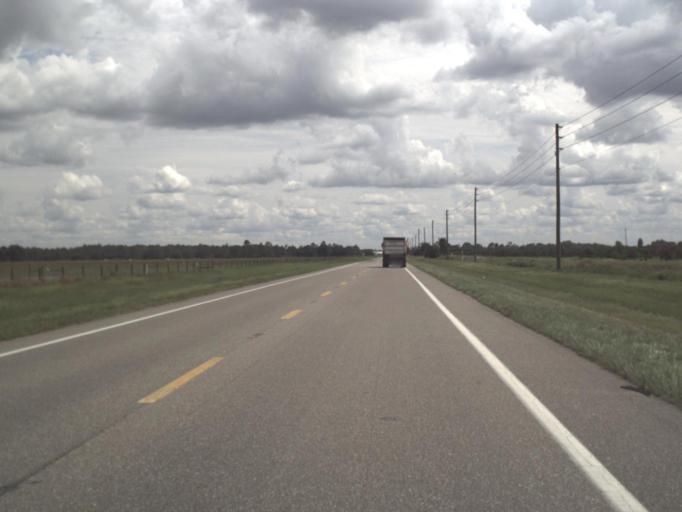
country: US
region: Florida
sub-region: DeSoto County
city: Nocatee
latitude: 27.0302
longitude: -81.7691
